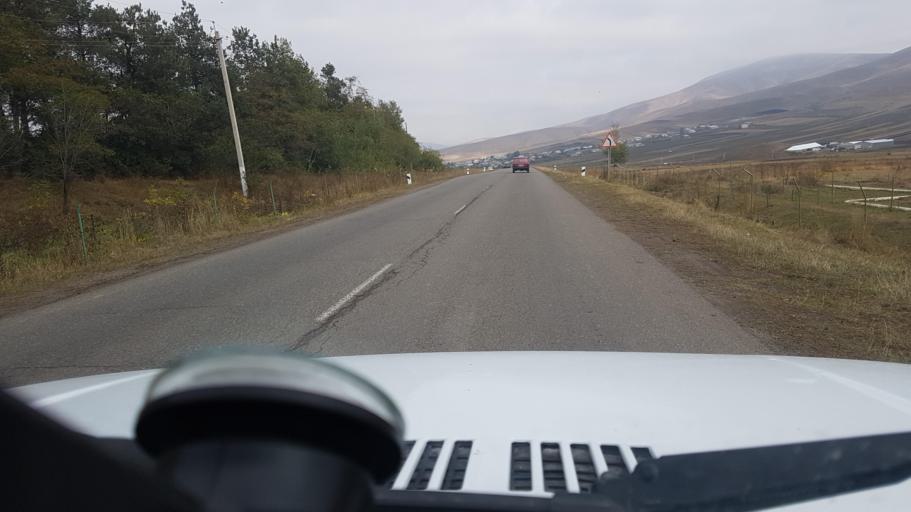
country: AZ
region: Gadabay Rayon
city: Ariqdam
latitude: 40.6230
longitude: 45.8148
